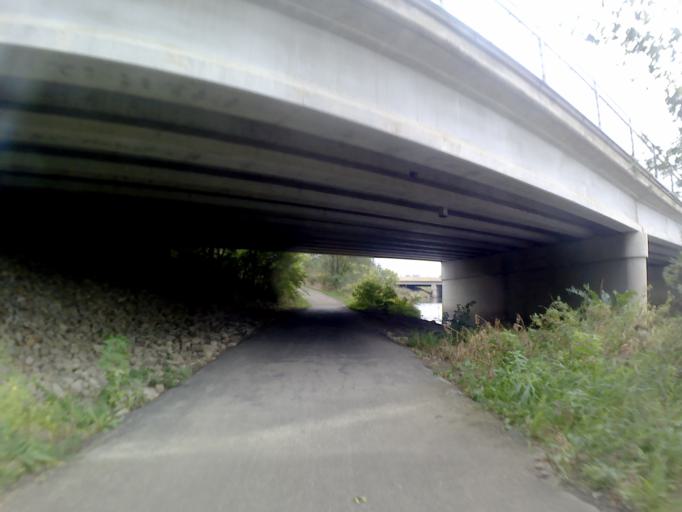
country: US
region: Illinois
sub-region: DuPage County
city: Warrenville
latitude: 41.8072
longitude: -88.1749
